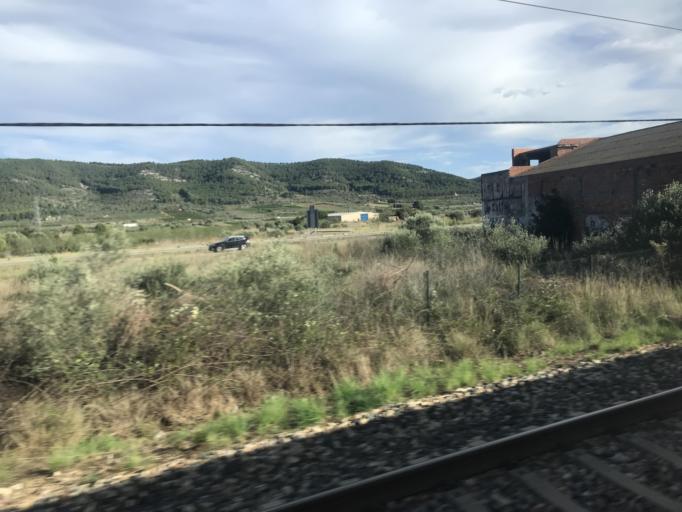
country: ES
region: Valencia
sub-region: Provincia de Castello
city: Alcala de Xivert
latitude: 40.3093
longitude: 0.2307
